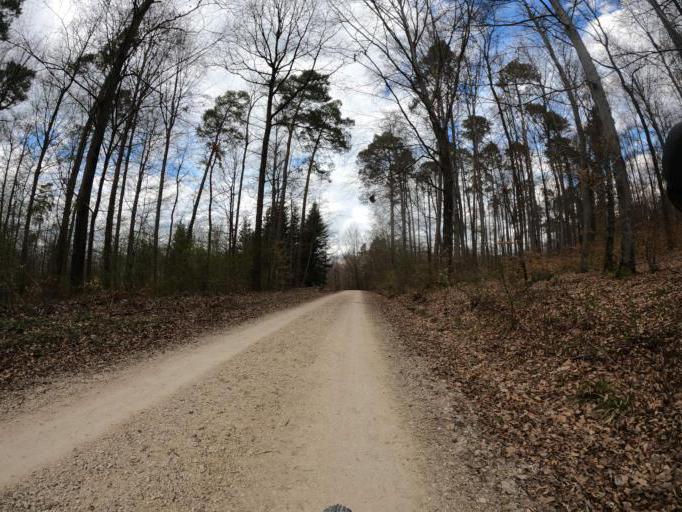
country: DE
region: Baden-Wuerttemberg
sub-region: Tuebingen Region
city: Gomaringen
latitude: 48.4594
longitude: 9.1294
